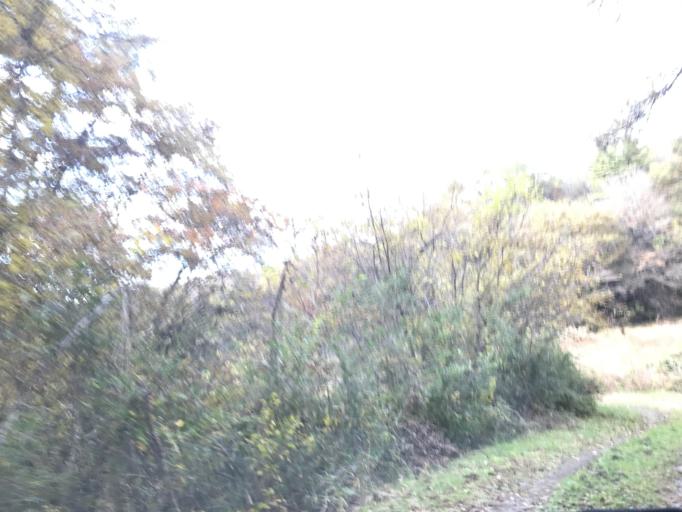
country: JP
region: Iwate
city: Ichinoseki
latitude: 38.8751
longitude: 141.1323
